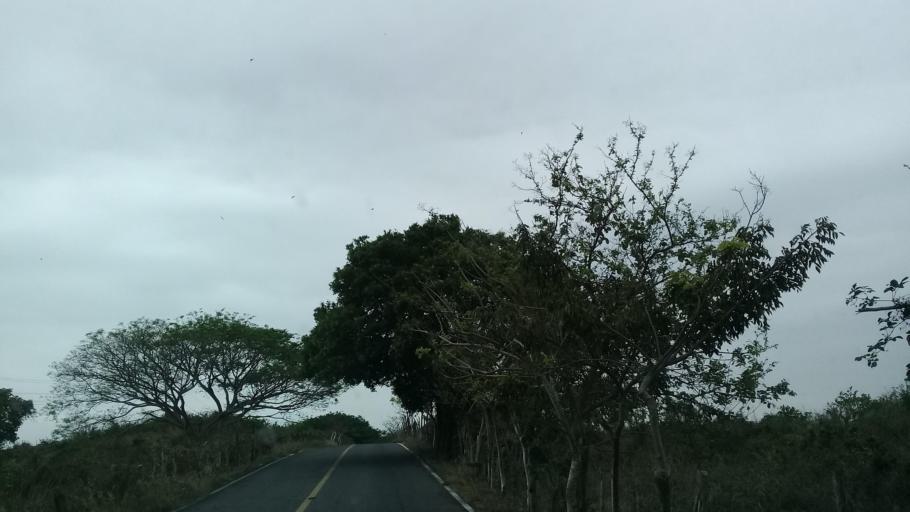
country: MX
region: Veracruz
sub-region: La Antigua
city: Nicolas Blanco (San Pancho)
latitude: 19.3368
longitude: -96.3266
